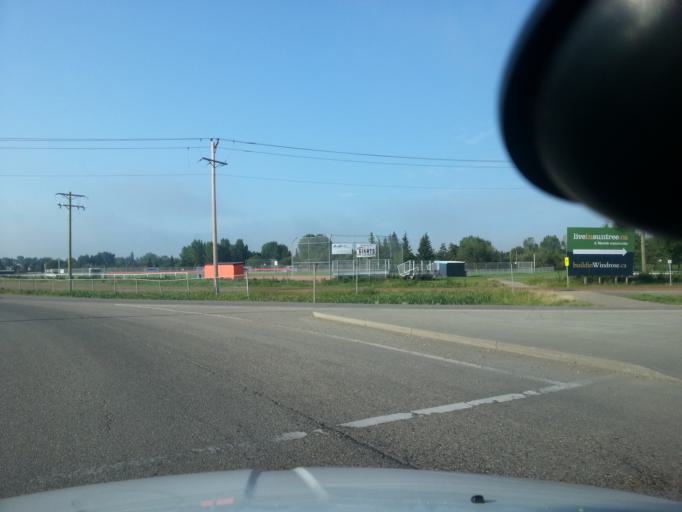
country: CA
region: Alberta
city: Leduc
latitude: 53.2647
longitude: -113.5653
